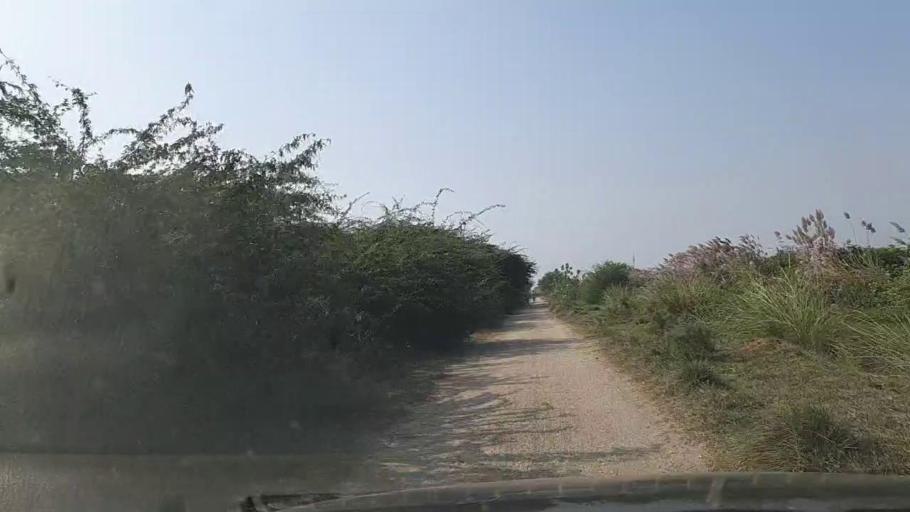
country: PK
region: Sindh
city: Gharo
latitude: 24.6965
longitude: 67.6194
